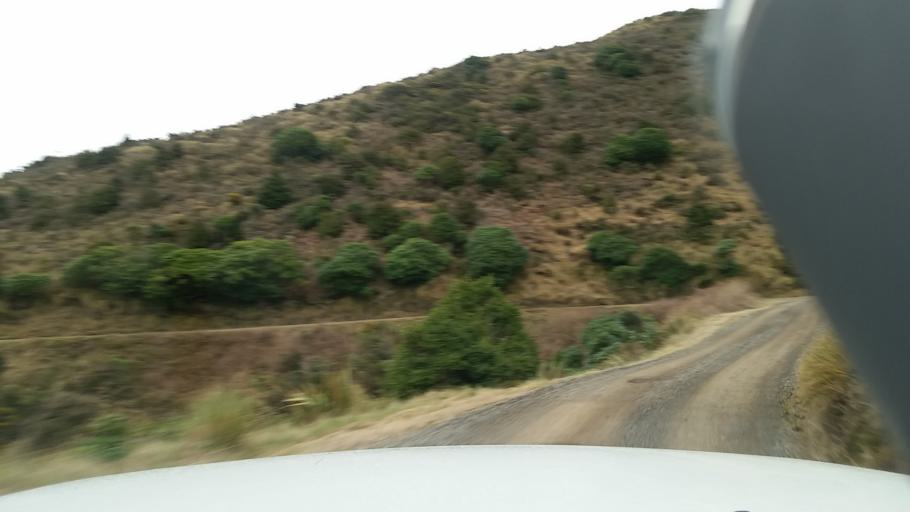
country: NZ
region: Canterbury
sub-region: Christchurch City
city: Christchurch
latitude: -43.8082
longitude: 172.8573
